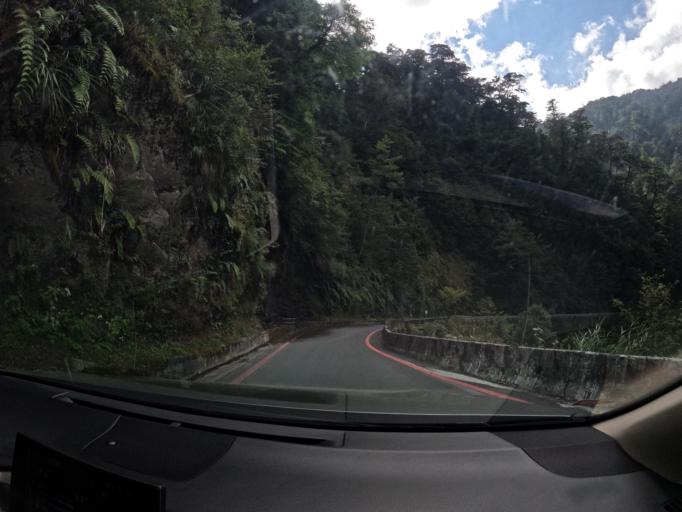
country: TW
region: Taiwan
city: Yujing
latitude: 23.2579
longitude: 120.9208
